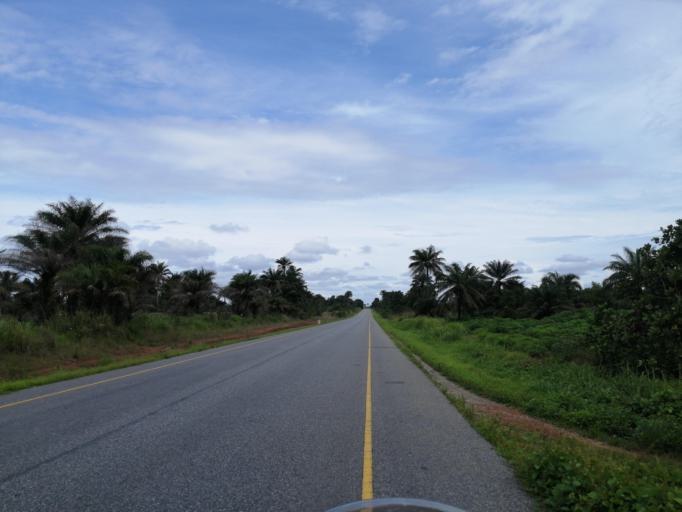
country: SL
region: Northern Province
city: Port Loko
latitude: 8.7405
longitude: -12.9412
